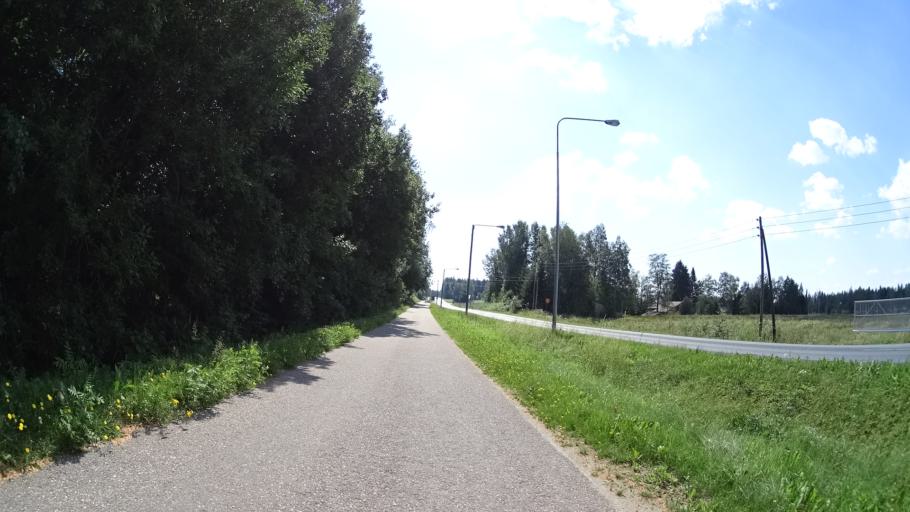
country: FI
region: Uusimaa
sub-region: Helsinki
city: Vantaa
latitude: 60.3387
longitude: 25.0043
